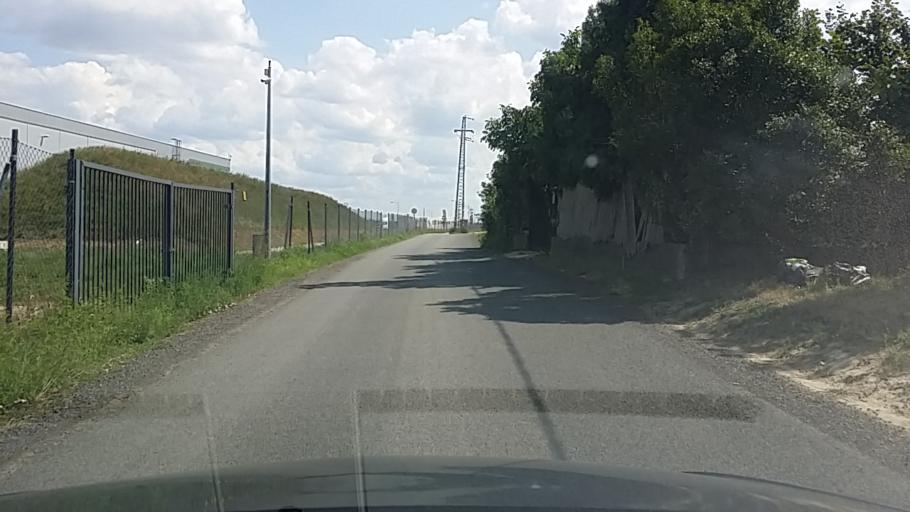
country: HU
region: Pest
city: Szigetszentmiklos
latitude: 47.3731
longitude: 19.0212
